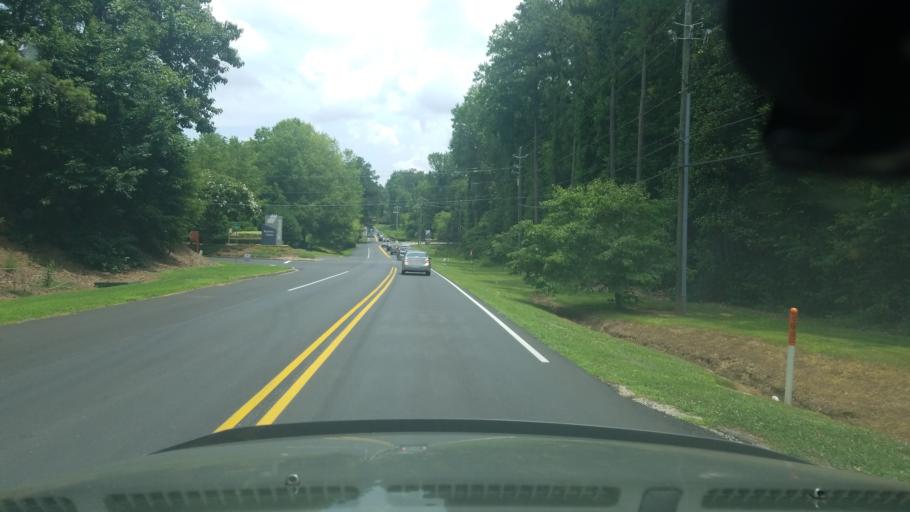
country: US
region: Georgia
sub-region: Fulton County
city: Johns Creek
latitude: 34.1001
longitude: -84.2099
